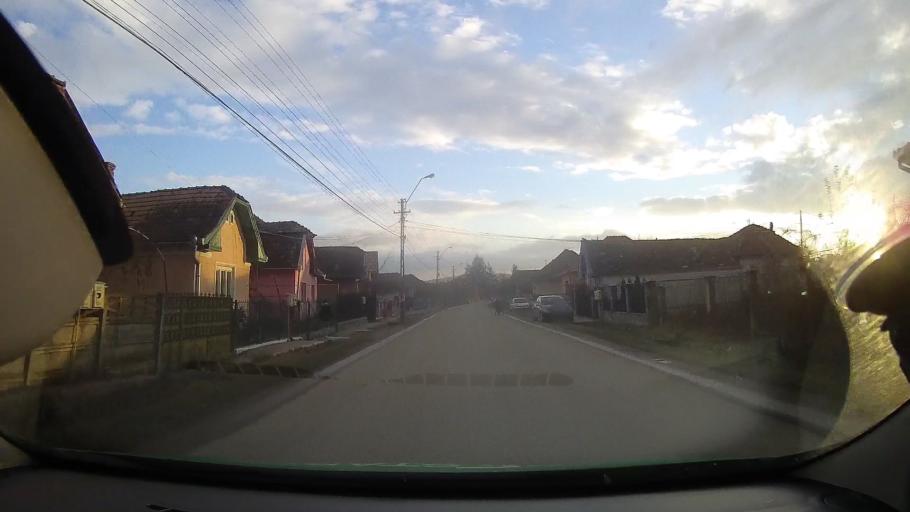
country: RO
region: Alba
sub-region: Oras Ocna Mures
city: Razboieni-Cetate
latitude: 46.4157
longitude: 23.8732
